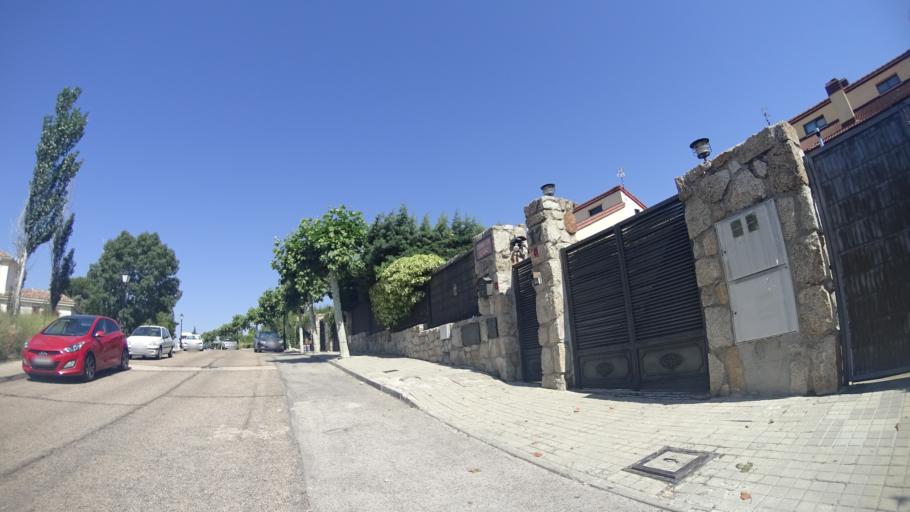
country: ES
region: Madrid
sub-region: Provincia de Madrid
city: Hoyo de Manzanares
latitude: 40.6071
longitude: -3.8993
